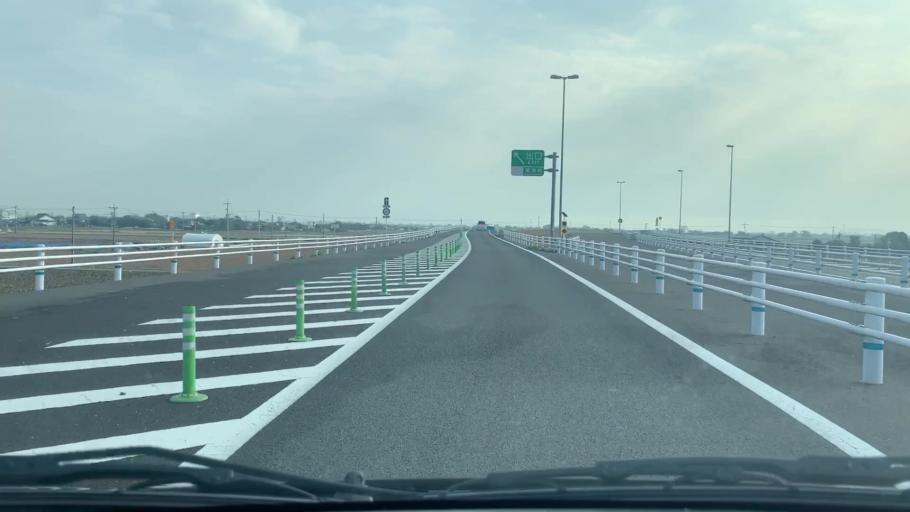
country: JP
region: Saga Prefecture
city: Saga-shi
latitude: 33.2315
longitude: 130.2542
